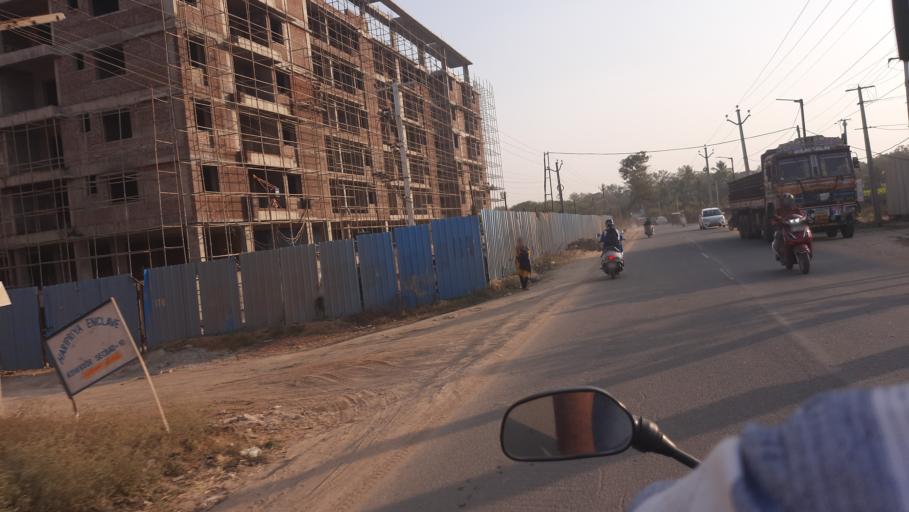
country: IN
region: Telangana
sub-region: Rangareddi
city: Secunderabad
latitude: 17.5192
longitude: 78.5407
